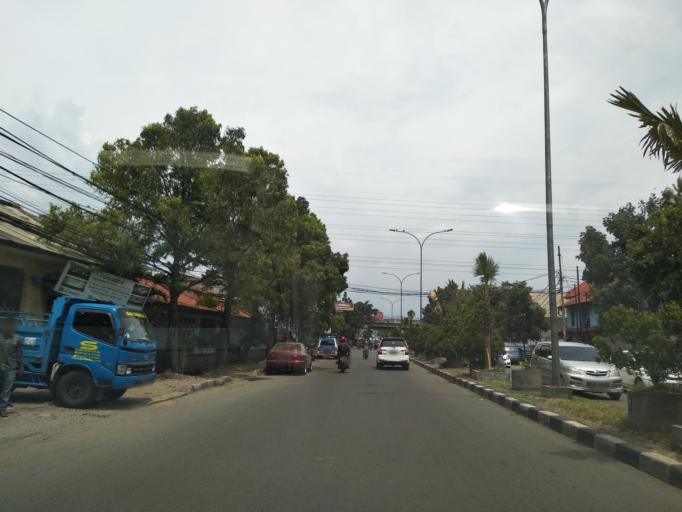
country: ID
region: West Java
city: Bandung
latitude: -6.9643
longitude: 107.6382
